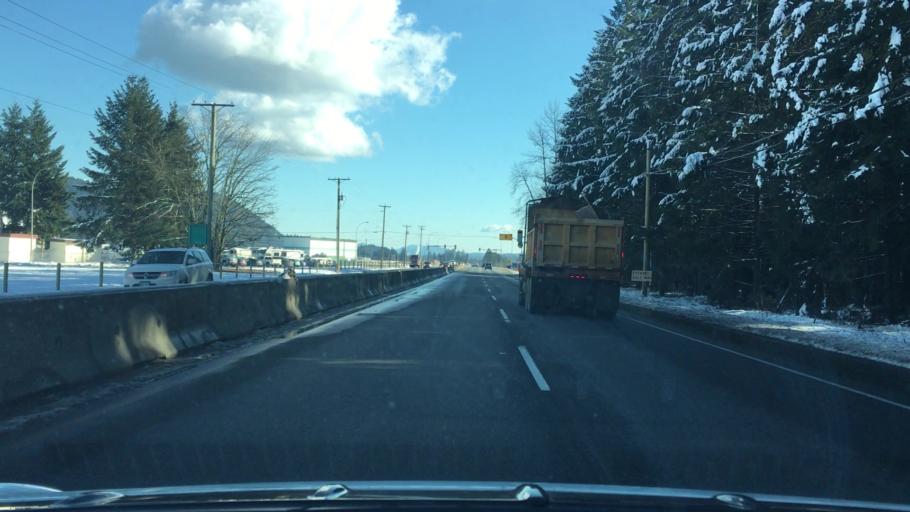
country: CA
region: British Columbia
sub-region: Cowichan Valley Regional District
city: Ladysmith
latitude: 49.0480
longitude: -123.8763
